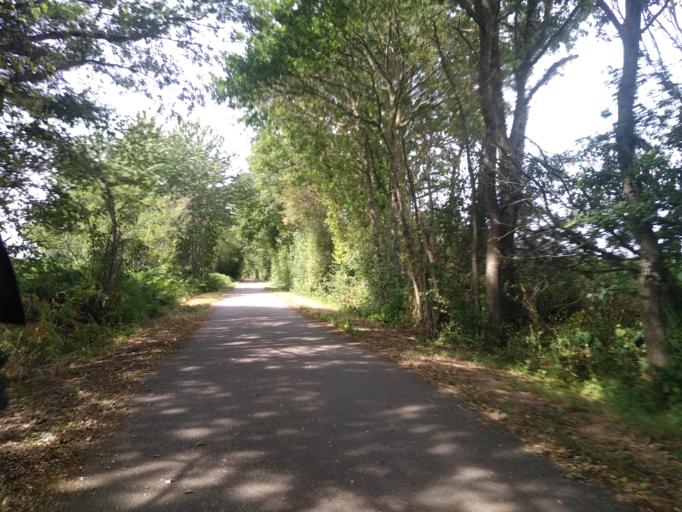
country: FR
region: Bourgogne
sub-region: Departement de Saone-et-Loire
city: Bourbon-Lancy
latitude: 46.6000
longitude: 3.7459
